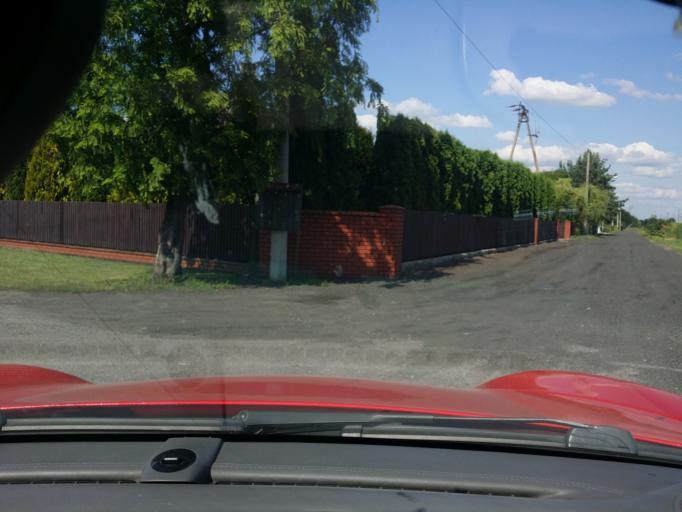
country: PL
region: Masovian Voivodeship
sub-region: Powiat radomski
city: Kowala
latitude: 51.3478
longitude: 21.0904
